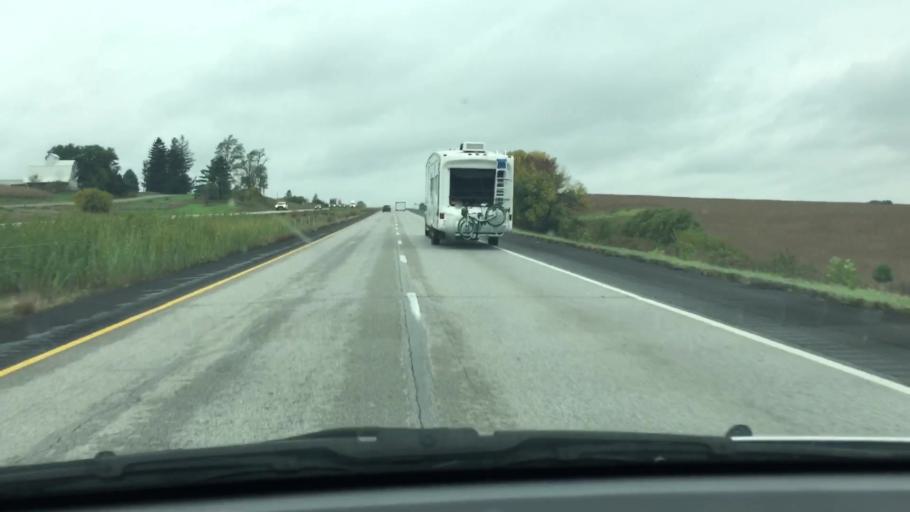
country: US
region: Iowa
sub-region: Johnson County
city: Tiffin
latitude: 41.6875
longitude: -91.8288
